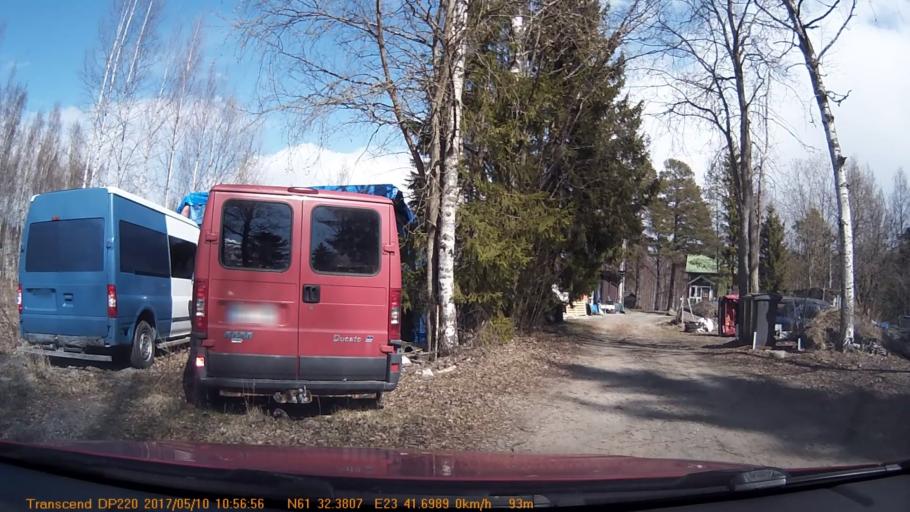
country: FI
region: Pirkanmaa
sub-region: Tampere
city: Yloejaervi
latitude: 61.5397
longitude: 23.6950
